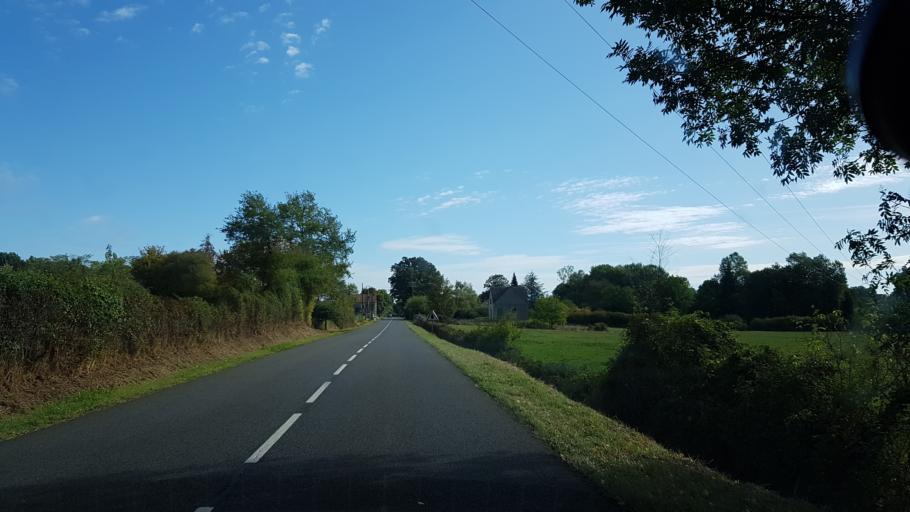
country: FR
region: Bourgogne
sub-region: Departement de la Nievre
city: Neuvy-sur-Loire
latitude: 47.5289
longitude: 2.8856
